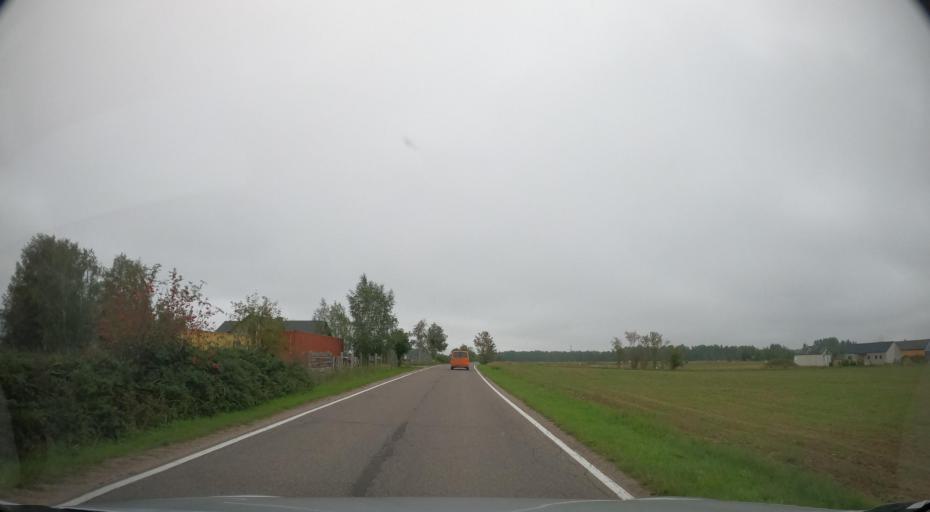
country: PL
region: Pomeranian Voivodeship
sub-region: Powiat wejherowski
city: Szemud
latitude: 54.5023
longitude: 18.1582
